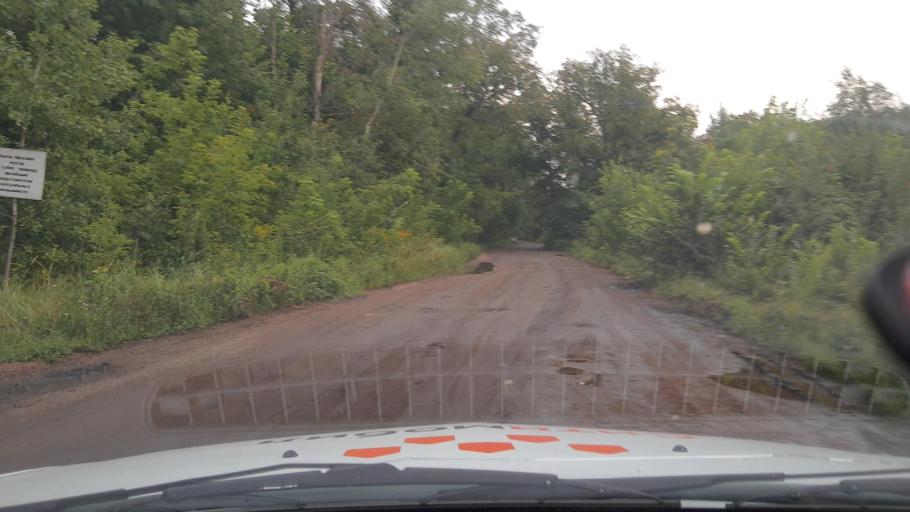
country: RU
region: Bashkortostan
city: Ufa
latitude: 54.5681
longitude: 55.9508
